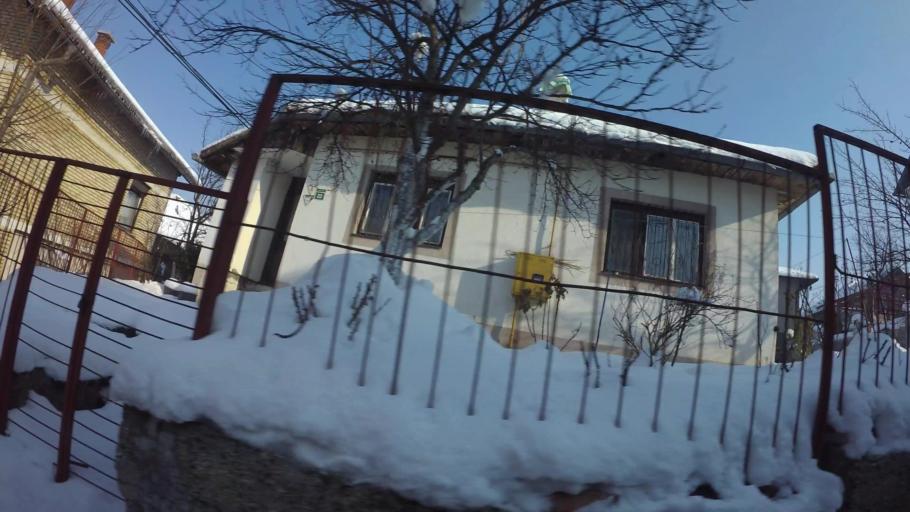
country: BA
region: Federation of Bosnia and Herzegovina
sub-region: Kanton Sarajevo
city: Sarajevo
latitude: 43.8425
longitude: 18.3650
